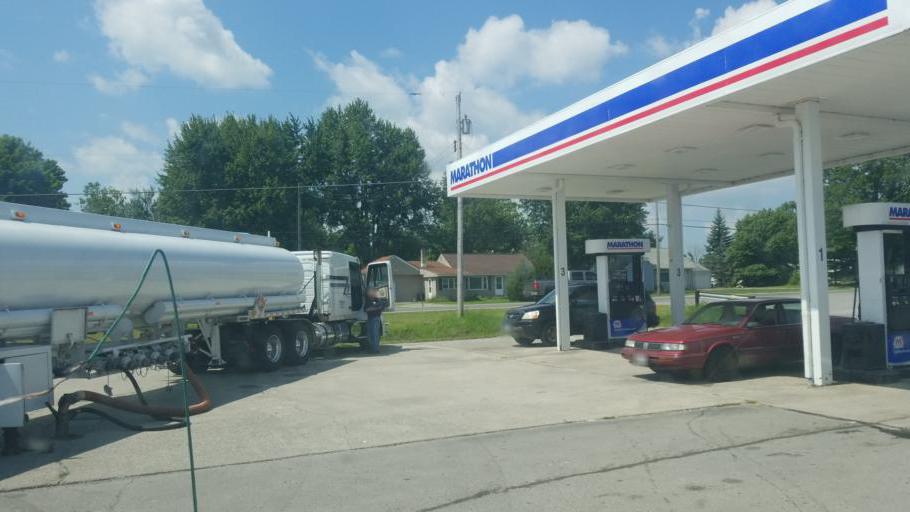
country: US
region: Ohio
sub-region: Allen County
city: Lima
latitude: 40.6970
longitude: -83.9841
